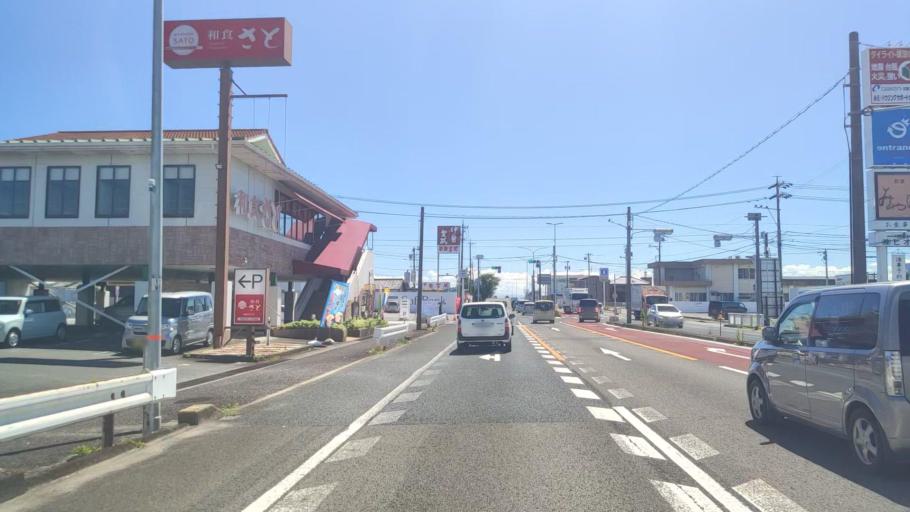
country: JP
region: Mie
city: Kawage
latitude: 34.8337
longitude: 136.5853
